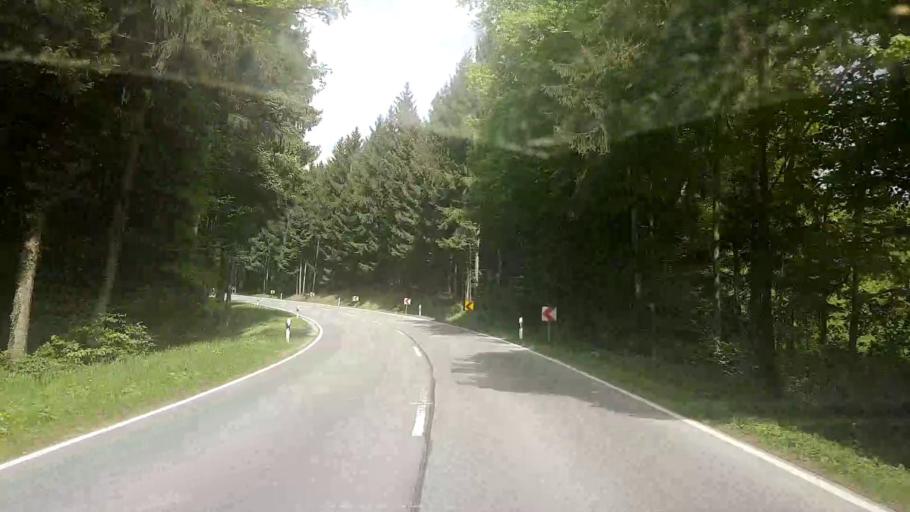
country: DE
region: Bavaria
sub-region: Upper Franconia
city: Lichtenfels
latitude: 50.1675
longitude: 11.0520
